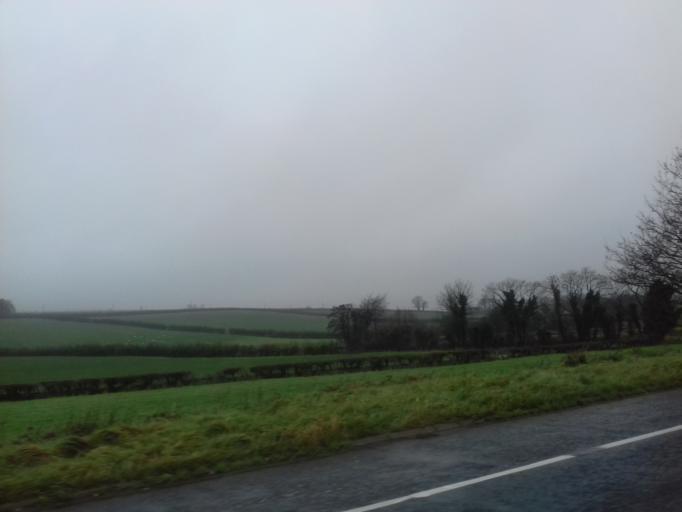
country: GB
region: Northern Ireland
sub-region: Strabane District
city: Sion Mills
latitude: 54.7524
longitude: -7.4473
